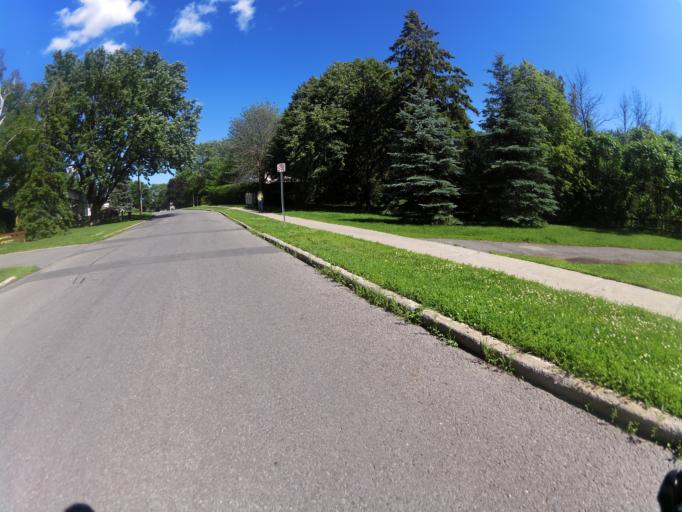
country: CA
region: Ontario
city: Bells Corners
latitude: 45.3292
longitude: -75.7859
